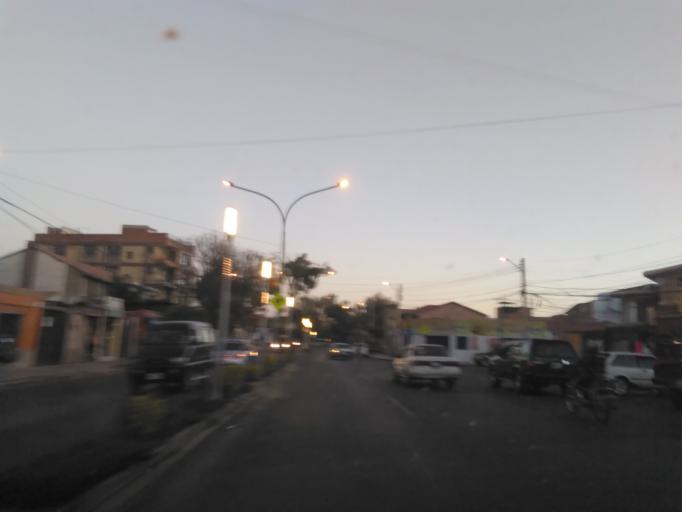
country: BO
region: Cochabamba
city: Cochabamba
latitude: -17.3902
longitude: -66.1706
